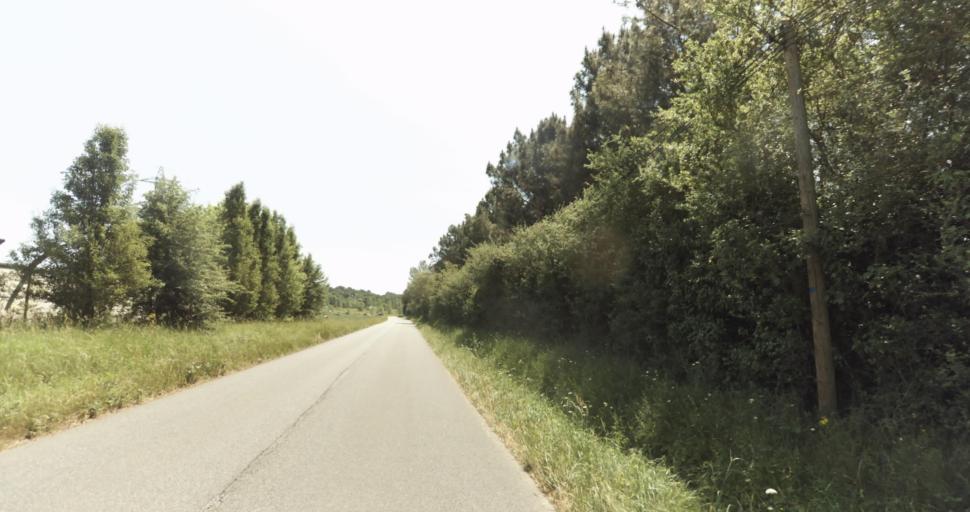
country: FR
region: Midi-Pyrenees
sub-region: Departement de la Haute-Garonne
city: La Salvetat-Saint-Gilles
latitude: 43.5974
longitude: 1.2743
